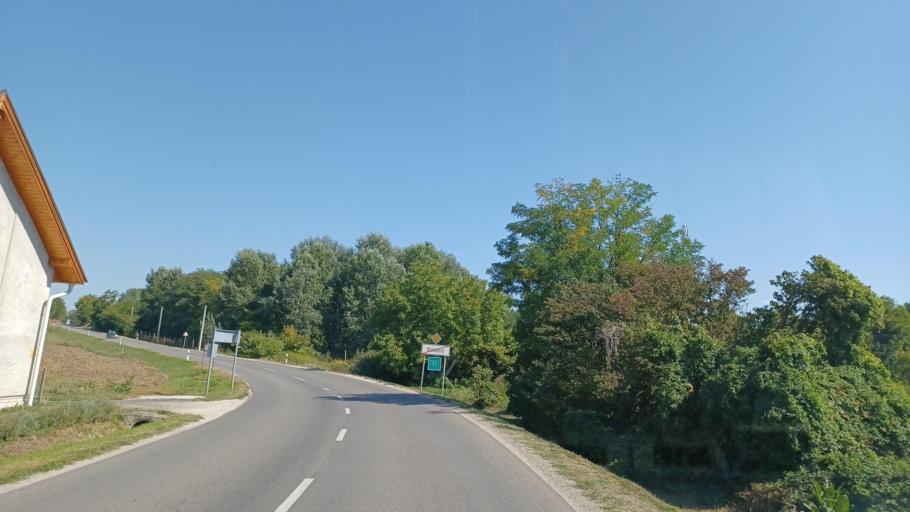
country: HU
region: Tolna
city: Nagydorog
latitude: 46.6800
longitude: 18.6675
